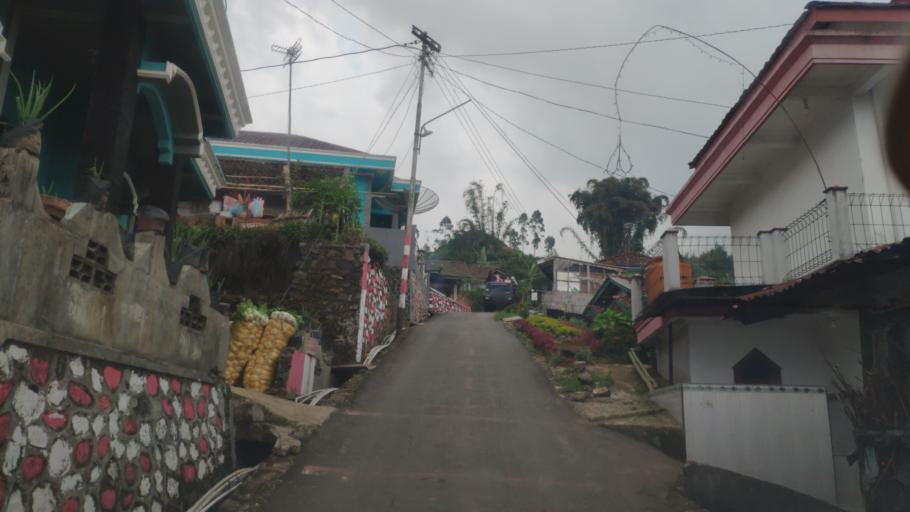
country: ID
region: Central Java
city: Wonosobo
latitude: -7.2445
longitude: 109.7949
